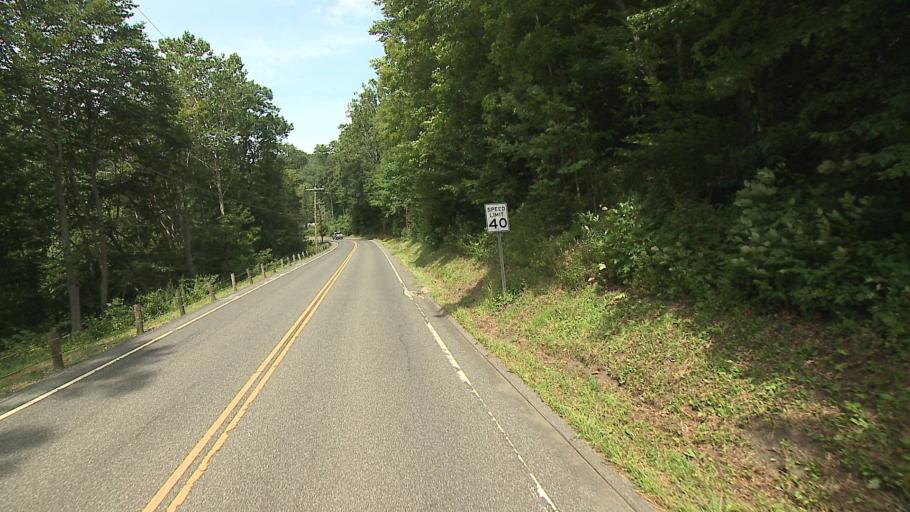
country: US
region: Connecticut
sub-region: Litchfield County
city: Woodbury
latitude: 41.5742
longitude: -73.2225
